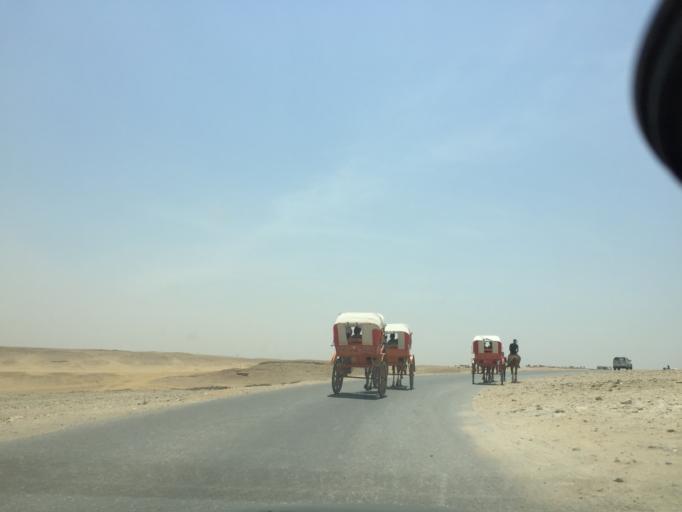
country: EG
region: Al Jizah
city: Al Jizah
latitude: 29.9736
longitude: 31.1259
